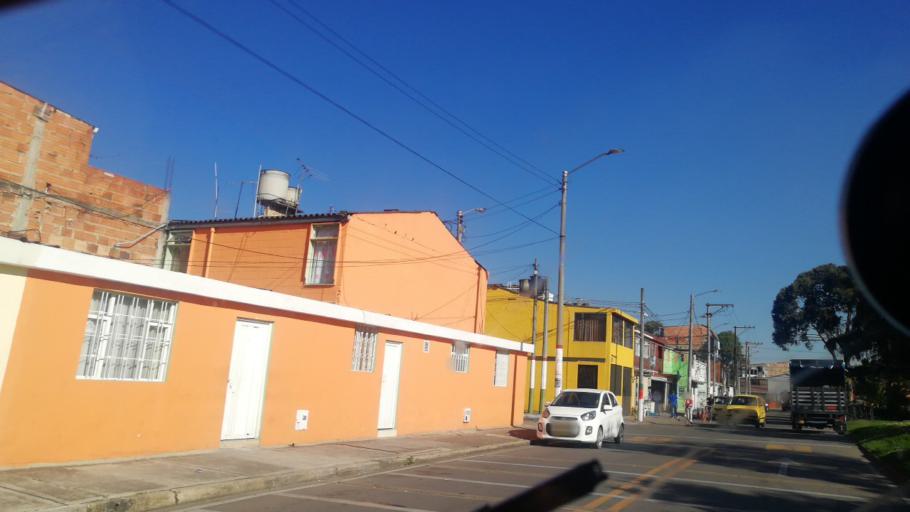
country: CO
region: Bogota D.C.
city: Bogota
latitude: 4.6225
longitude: -74.1424
